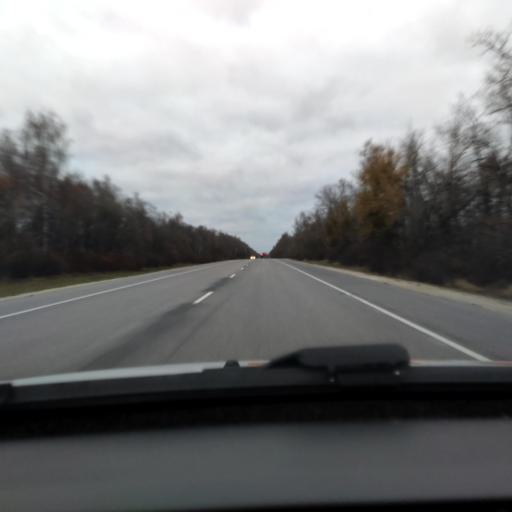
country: RU
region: Lipetsk
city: Khlevnoye
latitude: 52.2787
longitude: 39.1681
